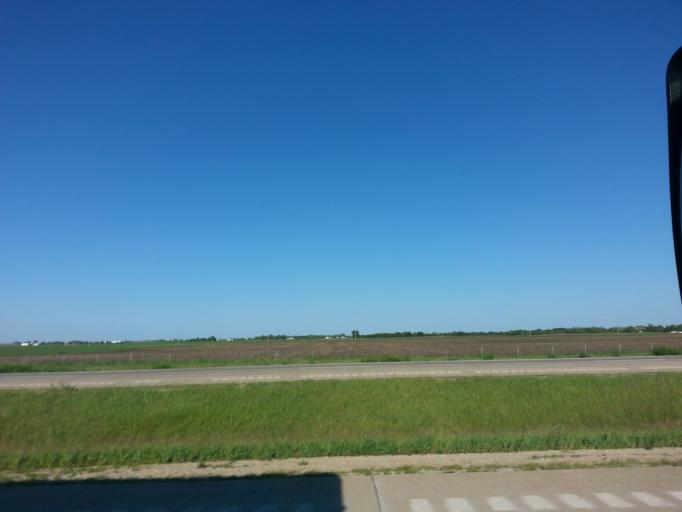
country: US
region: Illinois
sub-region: Woodford County
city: El Paso
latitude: 40.6854
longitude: -89.0290
